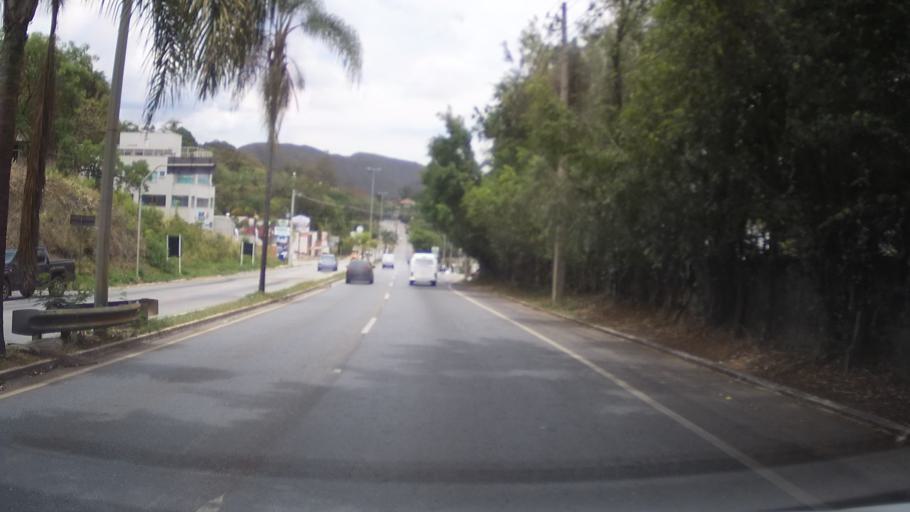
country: BR
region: Minas Gerais
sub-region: Nova Lima
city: Nova Lima
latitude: -19.9986
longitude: -43.8933
